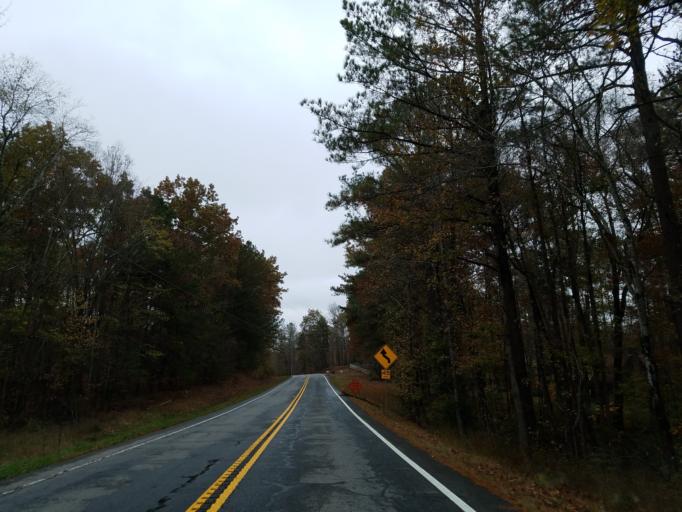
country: US
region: Georgia
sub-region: Cherokee County
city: Canton
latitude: 34.2266
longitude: -84.6168
